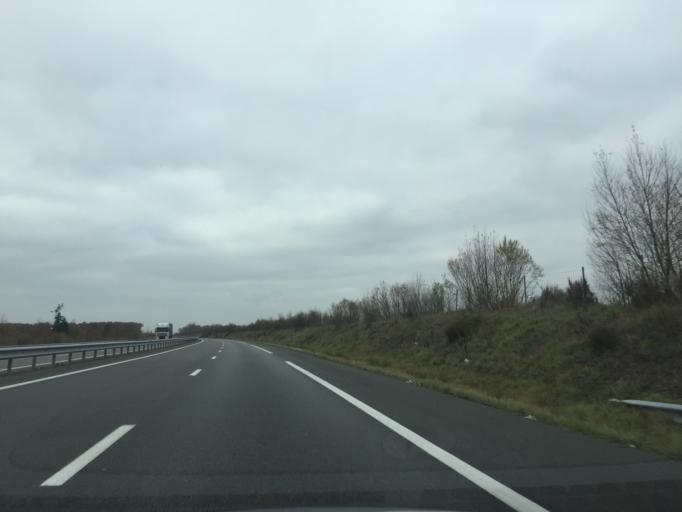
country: FR
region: Limousin
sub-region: Departement de la Creuse
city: Gouzon
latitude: 46.2164
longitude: 2.2862
